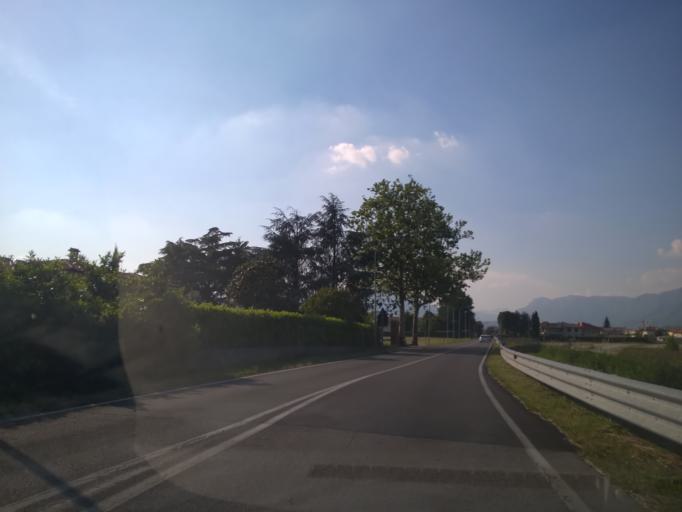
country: IT
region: Veneto
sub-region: Provincia di Vicenza
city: Thiene
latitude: 45.6949
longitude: 11.4952
